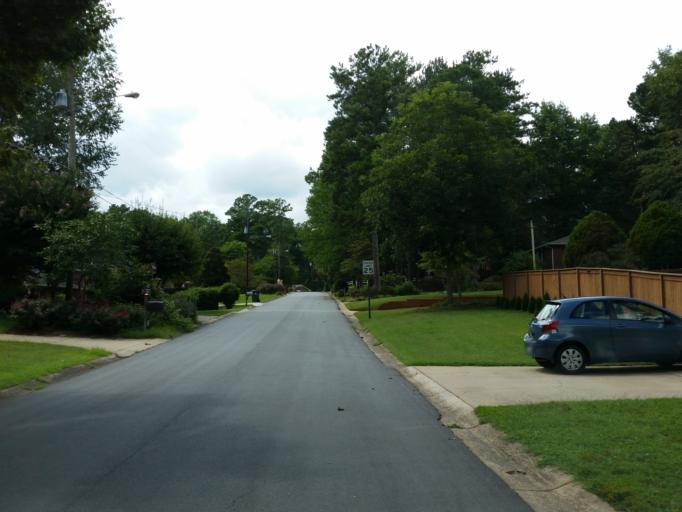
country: US
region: Georgia
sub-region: Cobb County
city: Marietta
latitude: 33.9655
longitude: -84.4833
